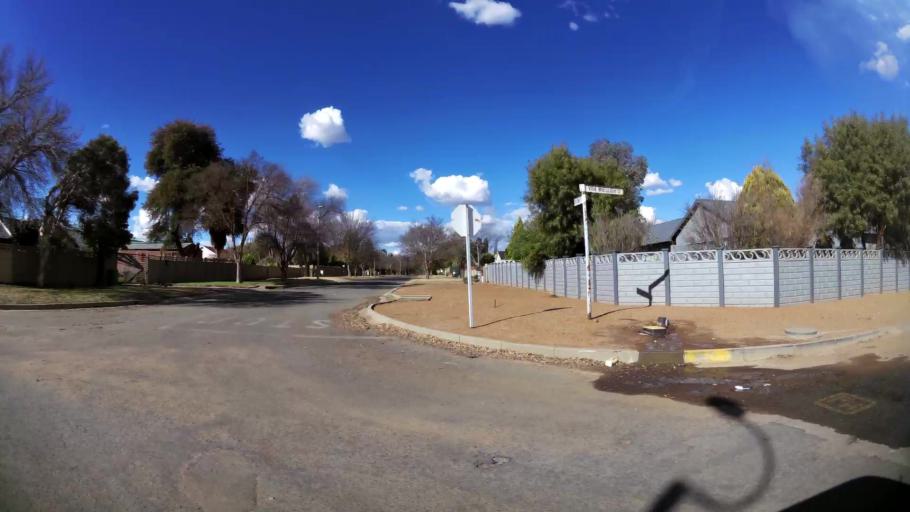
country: ZA
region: North-West
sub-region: Dr Kenneth Kaunda District Municipality
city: Klerksdorp
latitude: -26.8209
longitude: 26.6501
